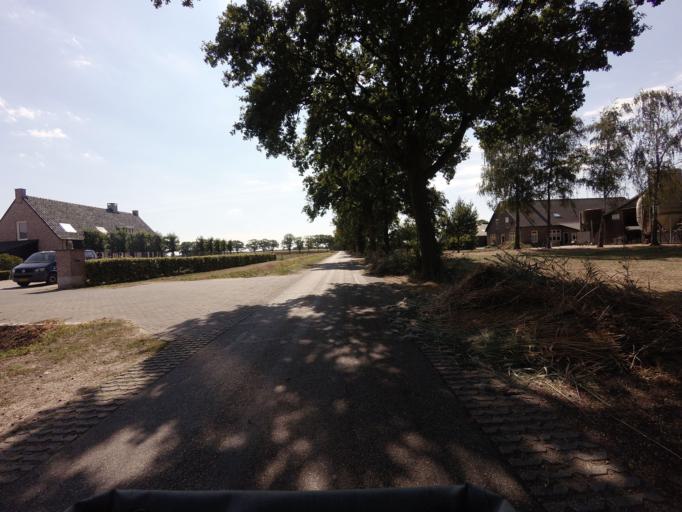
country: NL
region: North Brabant
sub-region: Gemeente Someren
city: Someren
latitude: 51.3563
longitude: 5.6681
